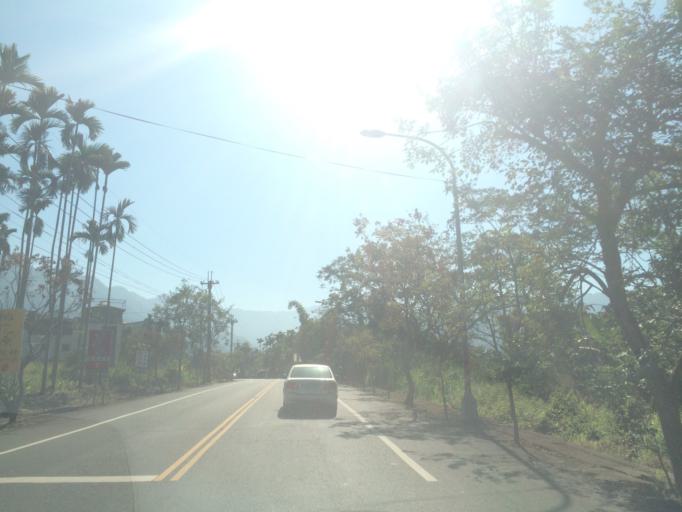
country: TW
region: Taiwan
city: Lugu
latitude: 23.7403
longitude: 120.7582
